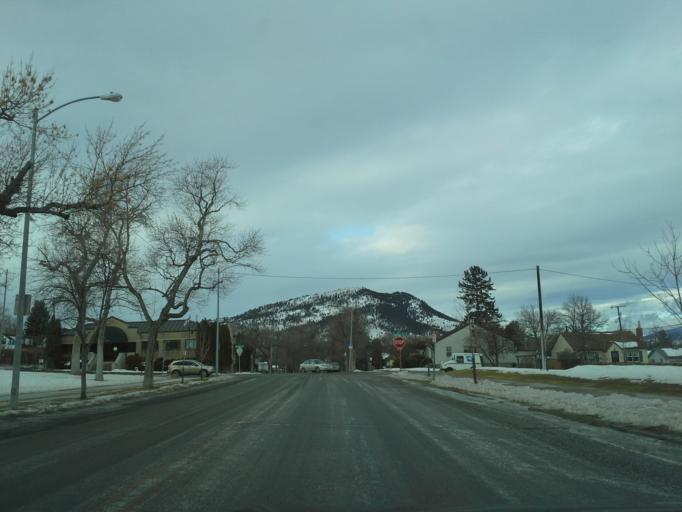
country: US
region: Montana
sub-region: Lewis and Clark County
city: Helena
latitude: 46.5868
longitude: -112.0193
